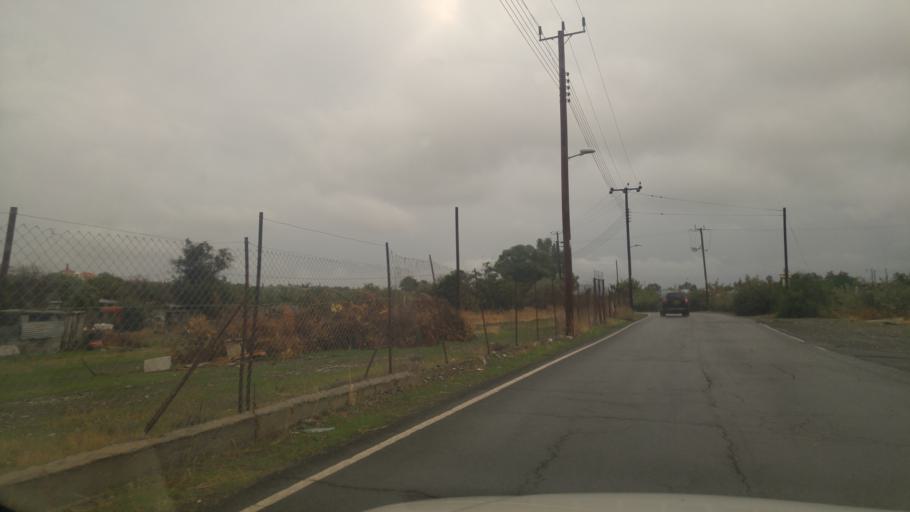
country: CY
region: Limassol
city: Mouttagiaka
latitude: 34.7148
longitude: 33.0887
